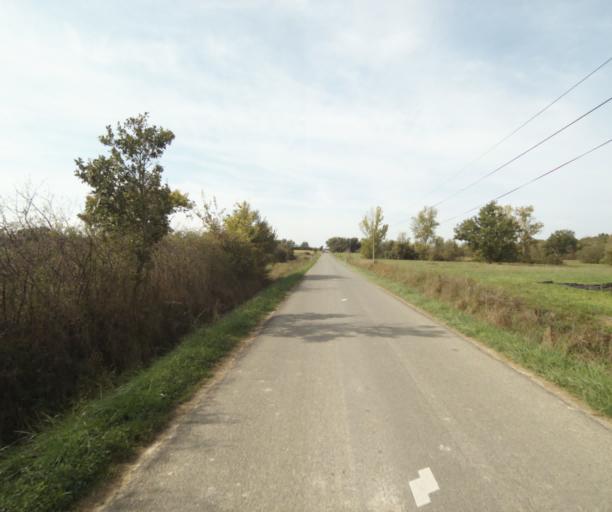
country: FR
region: Midi-Pyrenees
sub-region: Departement du Tarn-et-Garonne
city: Labastide-Saint-Pierre
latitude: 43.9012
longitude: 1.3760
